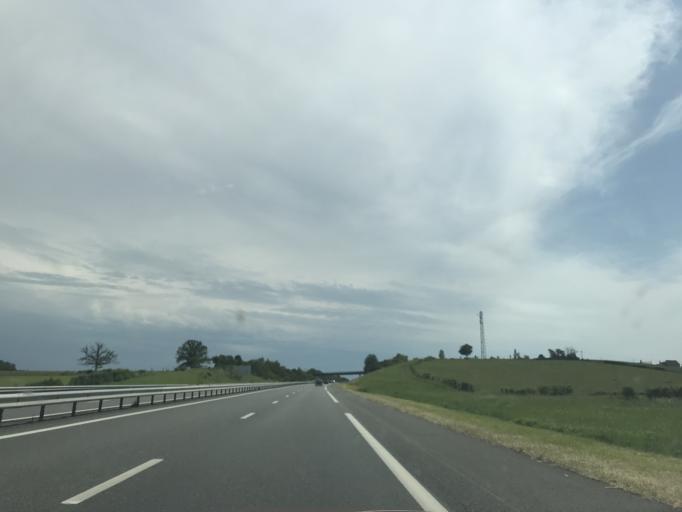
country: FR
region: Centre
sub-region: Departement du Cher
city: Orval
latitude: 46.7020
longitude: 2.4626
